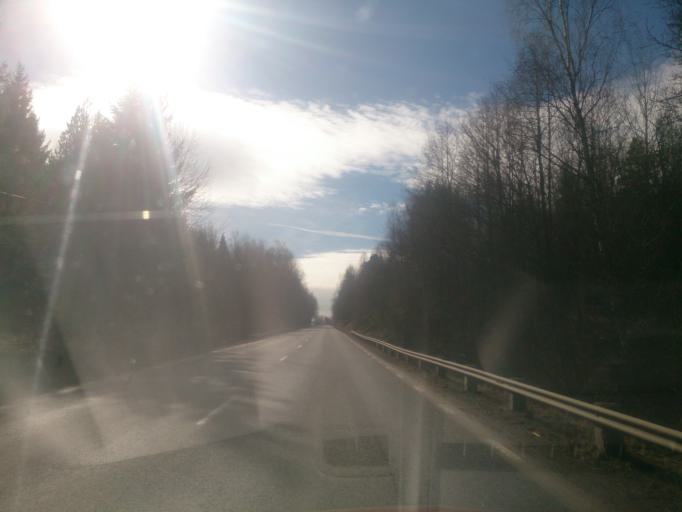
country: SE
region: OEstergoetland
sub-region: Finspangs Kommun
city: Finspang
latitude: 58.6386
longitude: 15.8217
